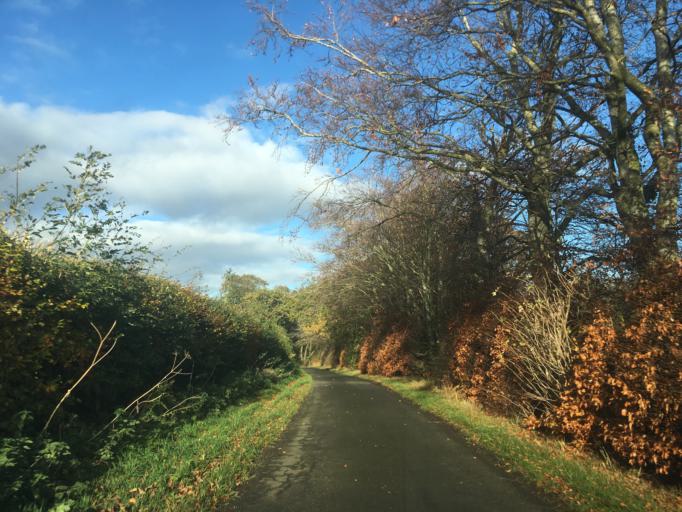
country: GB
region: Scotland
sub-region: East Lothian
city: Pencaitland
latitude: 55.8590
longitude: -2.8636
